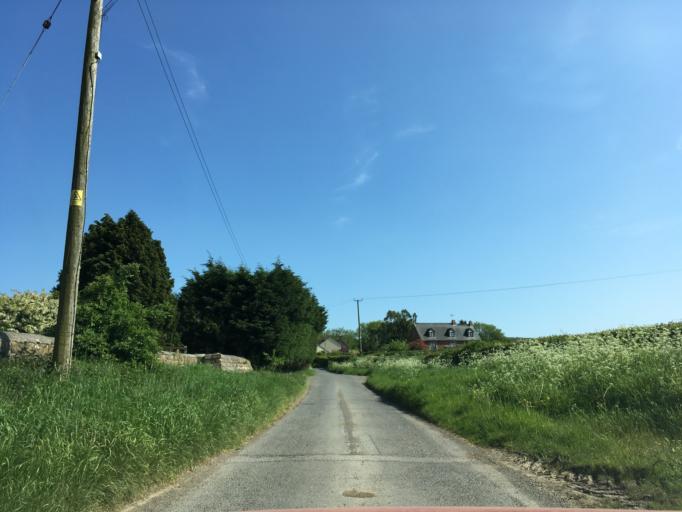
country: GB
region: England
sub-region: Gloucestershire
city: Dursley
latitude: 51.7184
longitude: -2.3814
